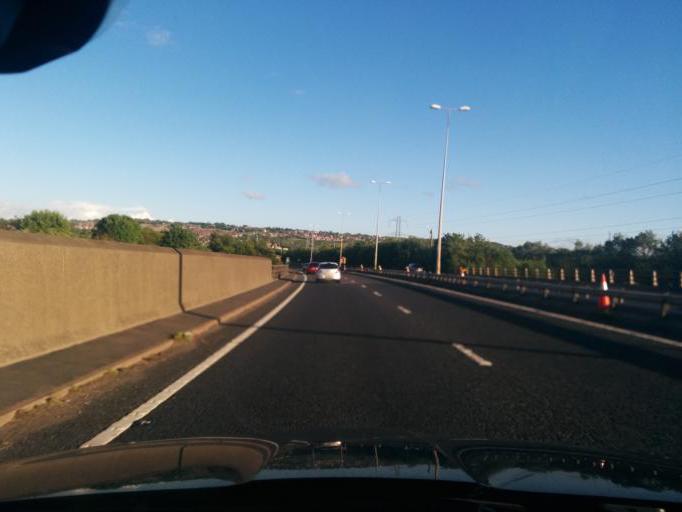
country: GB
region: England
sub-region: Gateshead
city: Blaydon-on-Tyne
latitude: 54.9651
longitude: -1.6974
